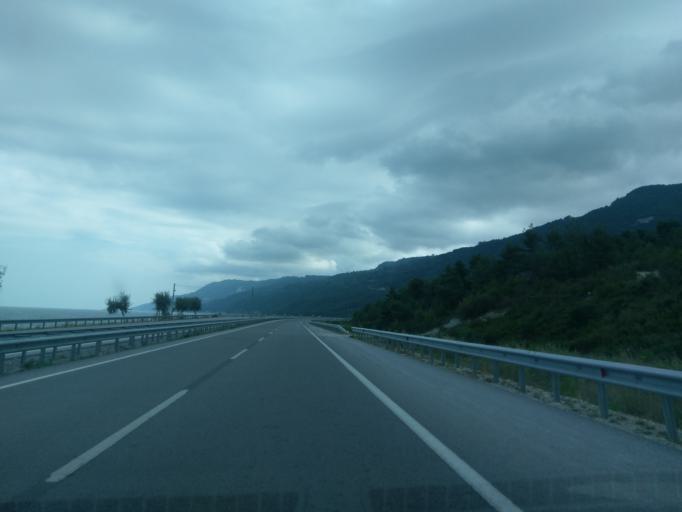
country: TR
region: Sinop
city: Dikmen
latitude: 41.7219
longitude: 35.2689
